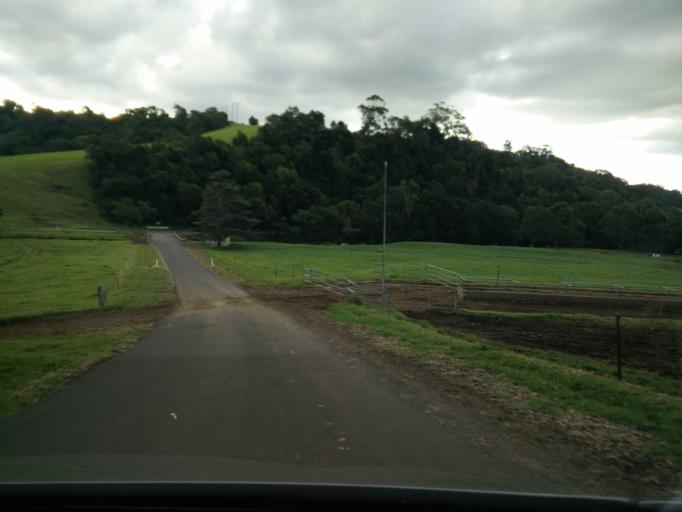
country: AU
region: New South Wales
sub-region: Kiama
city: Jamberoo
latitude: -34.6679
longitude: 150.7915
